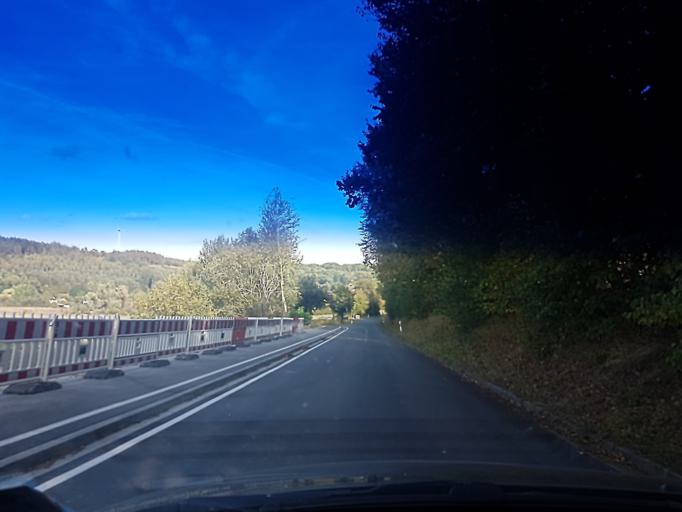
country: DE
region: Bavaria
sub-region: Regierungsbezirk Mittelfranken
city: Burghaslach
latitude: 49.7754
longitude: 10.5485
